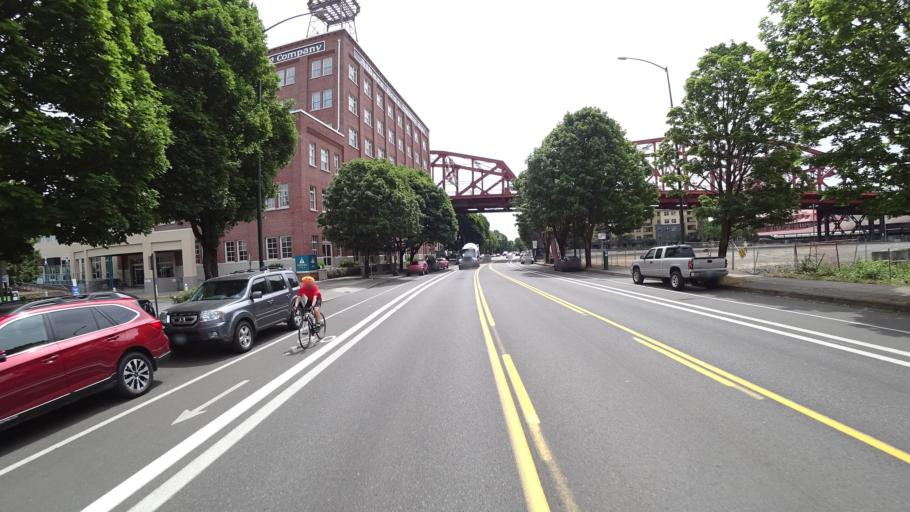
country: US
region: Oregon
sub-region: Multnomah County
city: Portland
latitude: 45.5312
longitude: -122.6770
